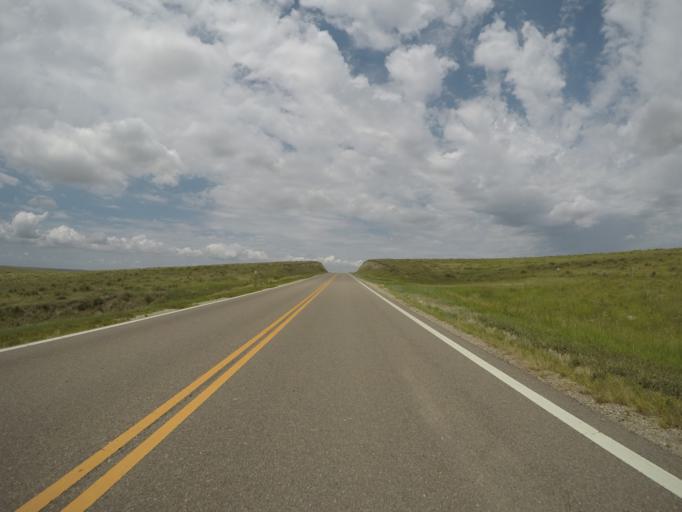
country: US
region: Kansas
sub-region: Rawlins County
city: Atwood
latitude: 39.7471
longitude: -101.0496
